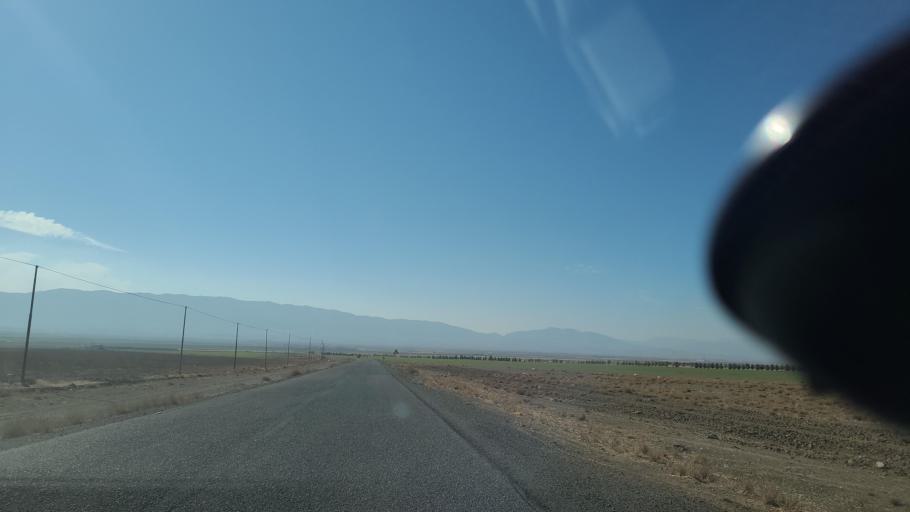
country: IR
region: Razavi Khorasan
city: Dowlatabad
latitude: 35.6113
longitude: 59.4698
